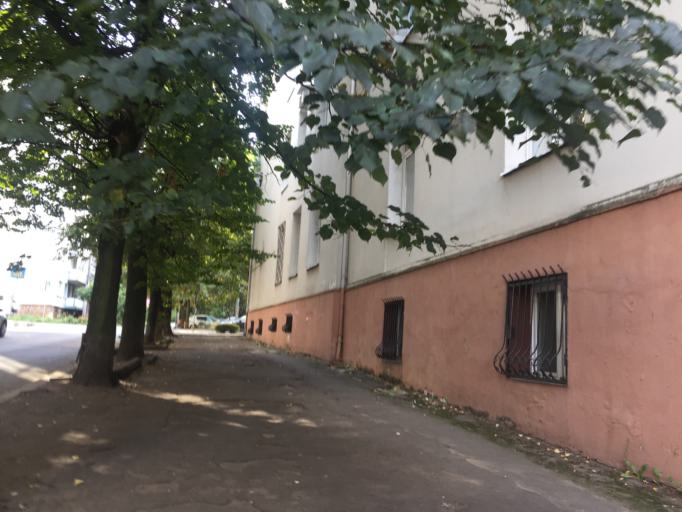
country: RU
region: Kaliningrad
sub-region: Gorod Kaliningrad
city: Kaliningrad
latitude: 54.6976
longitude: 20.5087
